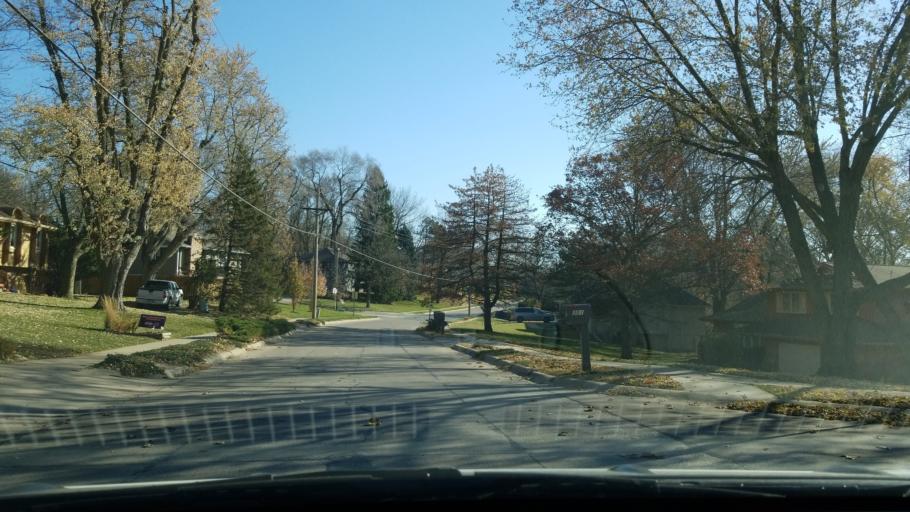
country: US
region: Nebraska
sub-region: Sarpy County
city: Bellevue
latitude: 41.1583
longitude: -95.9021
